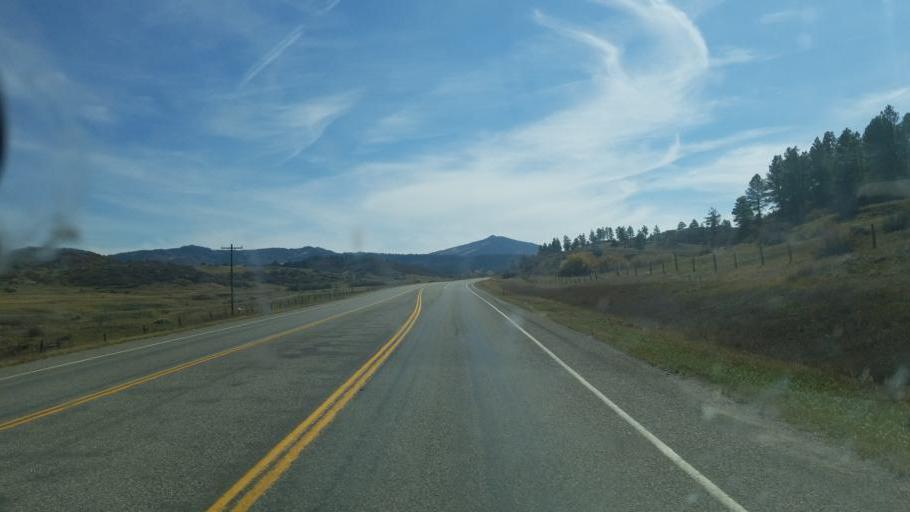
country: US
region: New Mexico
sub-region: Rio Arriba County
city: Dulce
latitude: 37.0156
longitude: -106.8081
